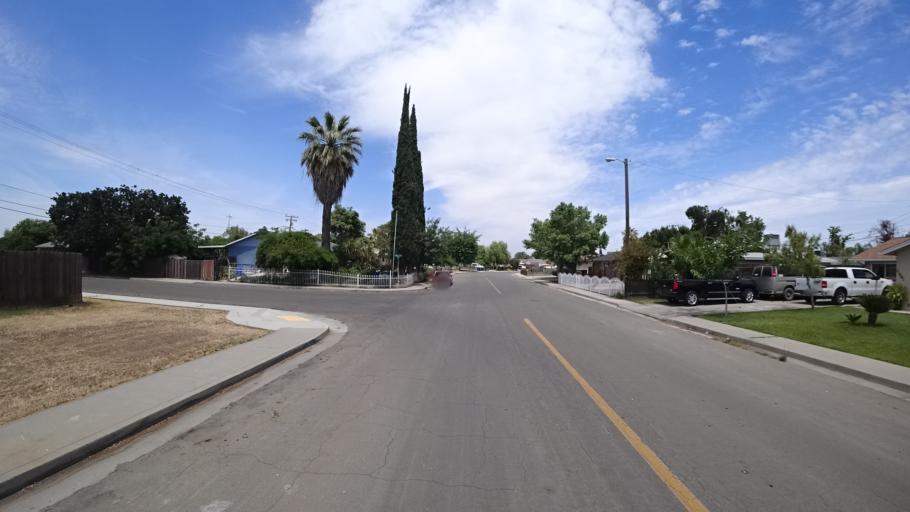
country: US
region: California
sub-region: Kings County
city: Armona
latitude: 36.3100
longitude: -119.7132
